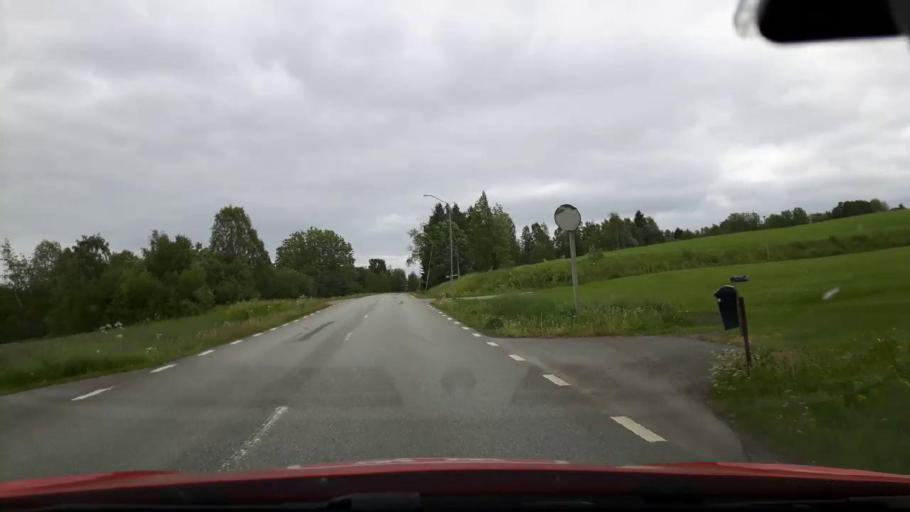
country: SE
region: Jaemtland
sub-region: Stroemsunds Kommun
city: Stroemsund
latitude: 63.5769
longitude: 15.3715
